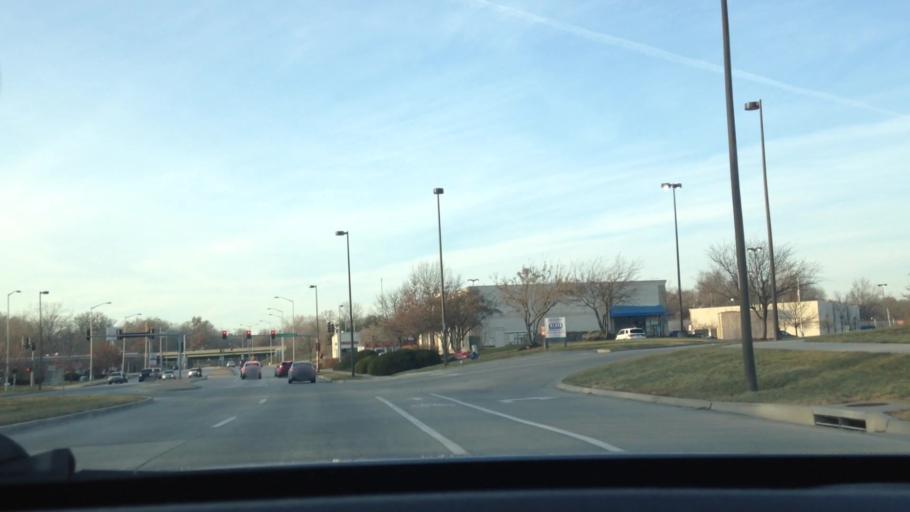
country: US
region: Missouri
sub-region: Clay County
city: Gladstone
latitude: 39.1719
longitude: -94.5339
